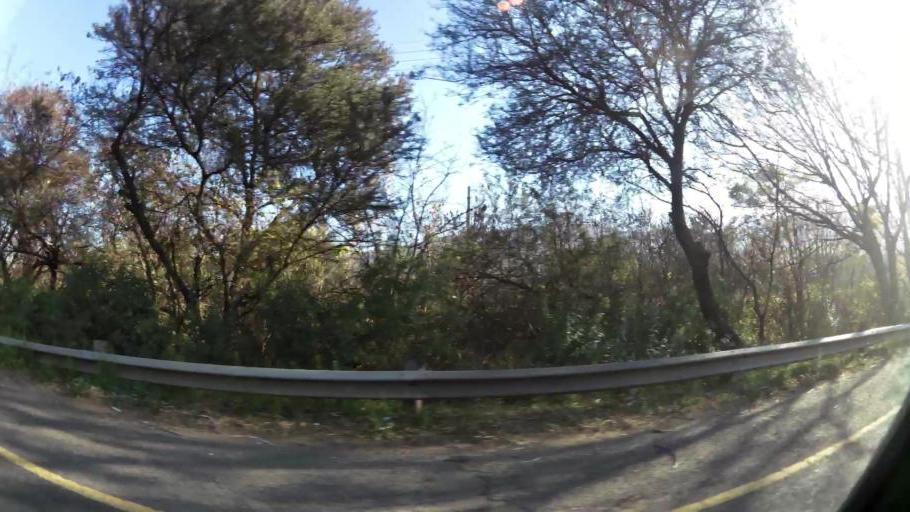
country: ZA
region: Gauteng
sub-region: City of Tshwane Metropolitan Municipality
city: Pretoria
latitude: -25.7010
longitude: 28.1735
